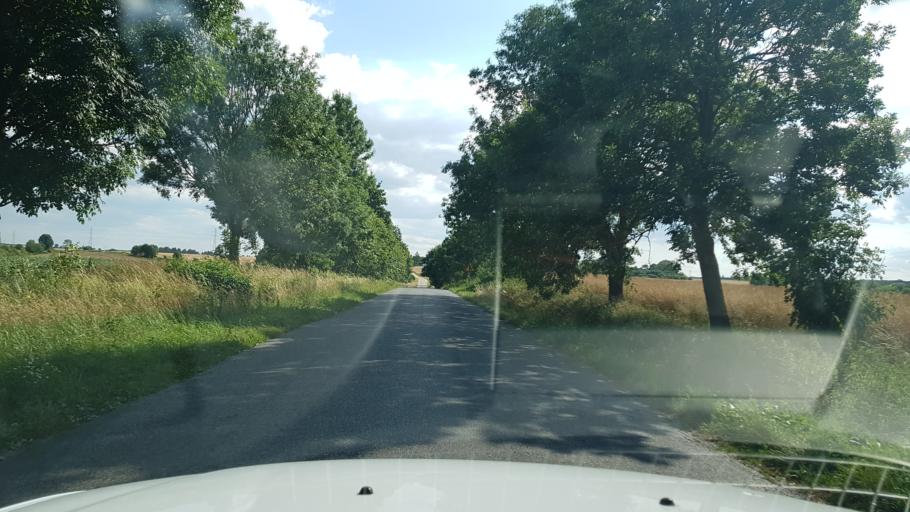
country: PL
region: West Pomeranian Voivodeship
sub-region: Powiat gryfinski
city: Stare Czarnowo
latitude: 53.2992
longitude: 14.8061
